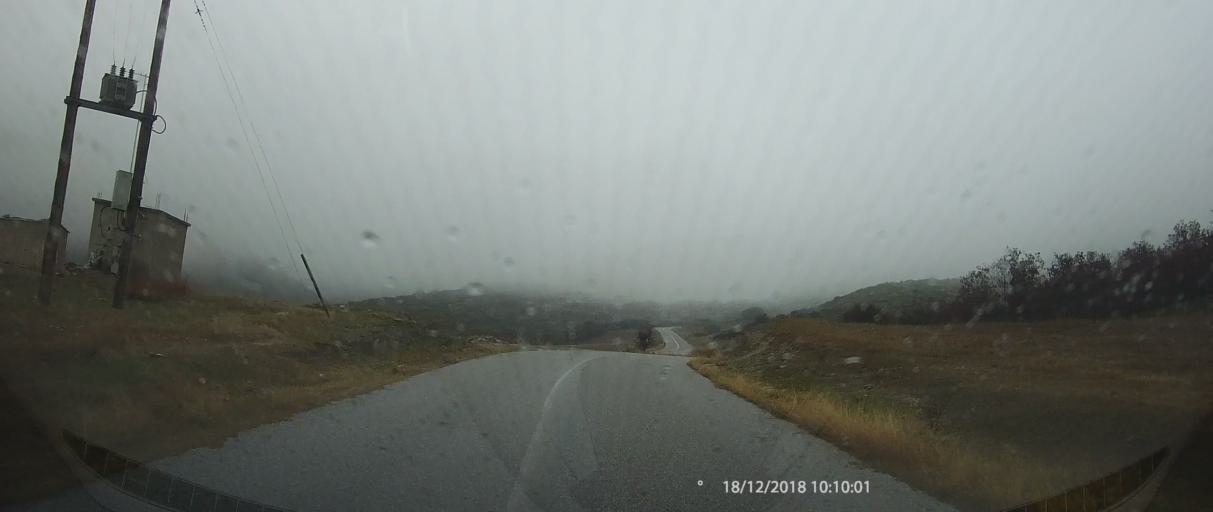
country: GR
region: Thessaly
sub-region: Nomos Larisis
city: Livadi
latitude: 40.0865
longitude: 22.2134
